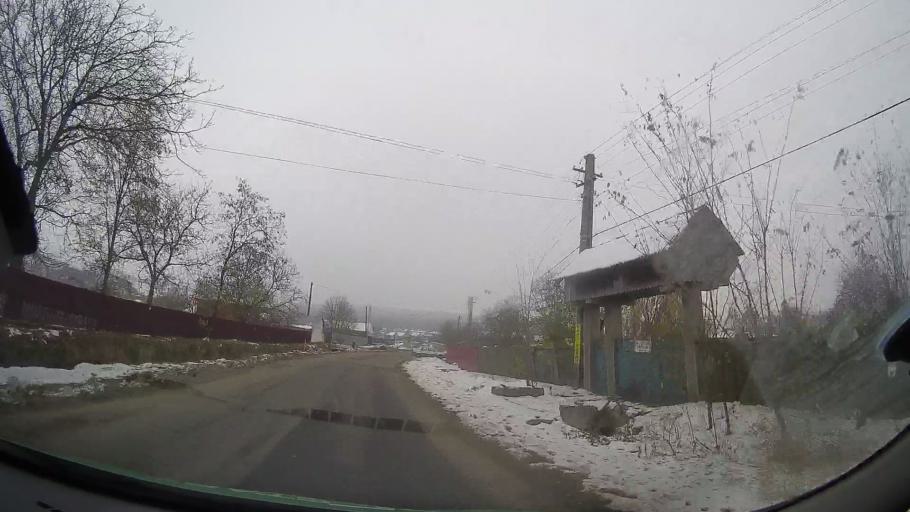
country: RO
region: Bacau
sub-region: Comuna Podu Turcului
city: Podu Turcului
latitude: 46.2079
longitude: 27.3788
